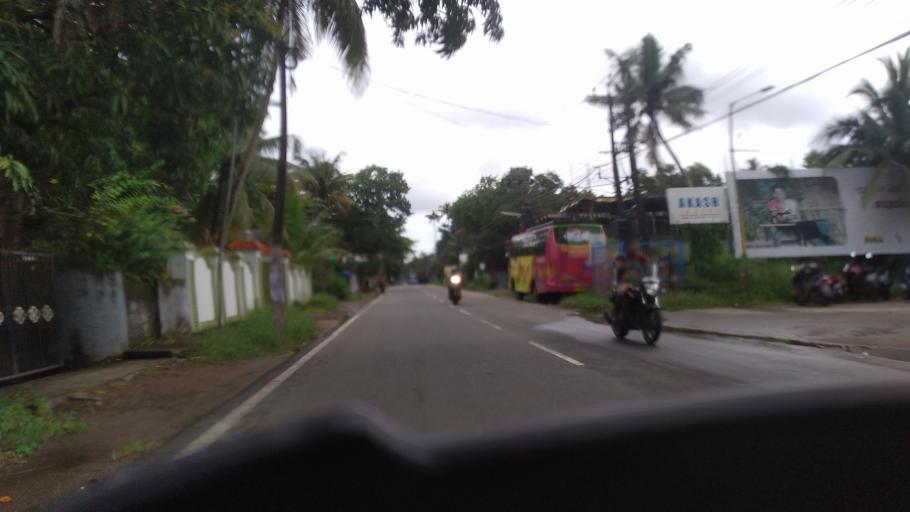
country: IN
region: Kerala
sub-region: Ernakulam
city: Elur
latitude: 10.0981
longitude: 76.2057
